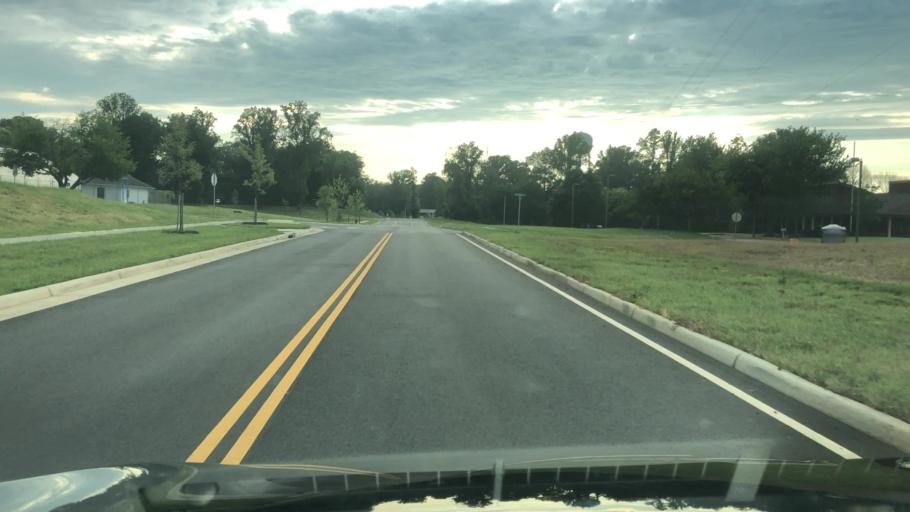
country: US
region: Virginia
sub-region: Fauquier County
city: New Baltimore
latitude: 38.7453
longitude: -77.6808
